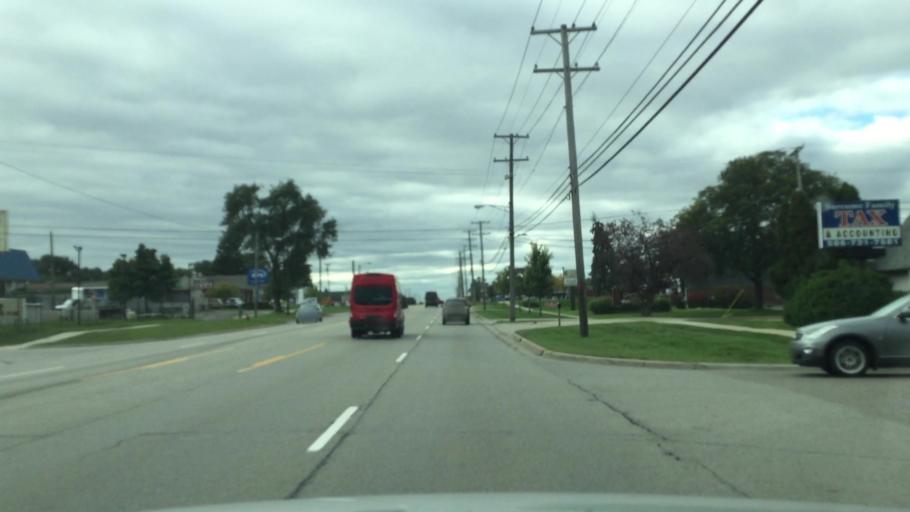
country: US
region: Michigan
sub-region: Macomb County
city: Shelby
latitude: 42.6509
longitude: -83.0333
